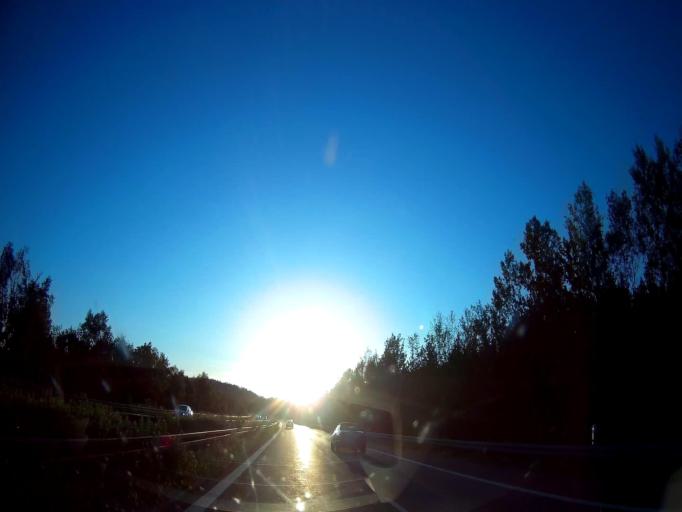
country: DE
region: Bavaria
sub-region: Regierungsbezirk Mittelfranken
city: Schnelldorf
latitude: 49.2084
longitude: 10.1848
